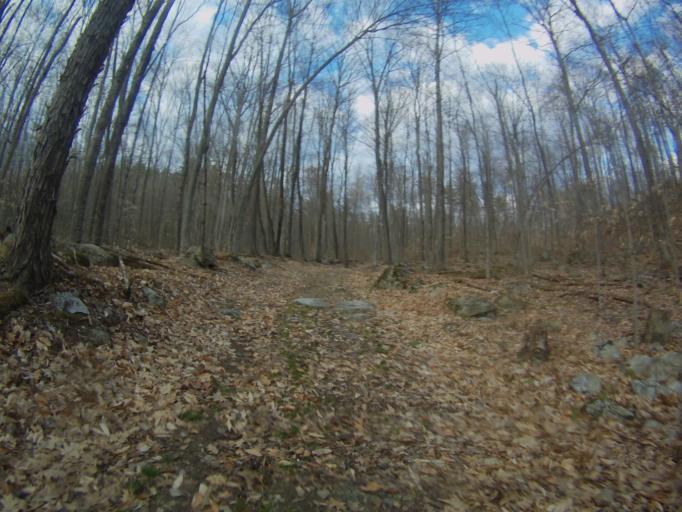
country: US
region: Vermont
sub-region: Rutland County
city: Brandon
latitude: 43.8413
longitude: -73.0411
